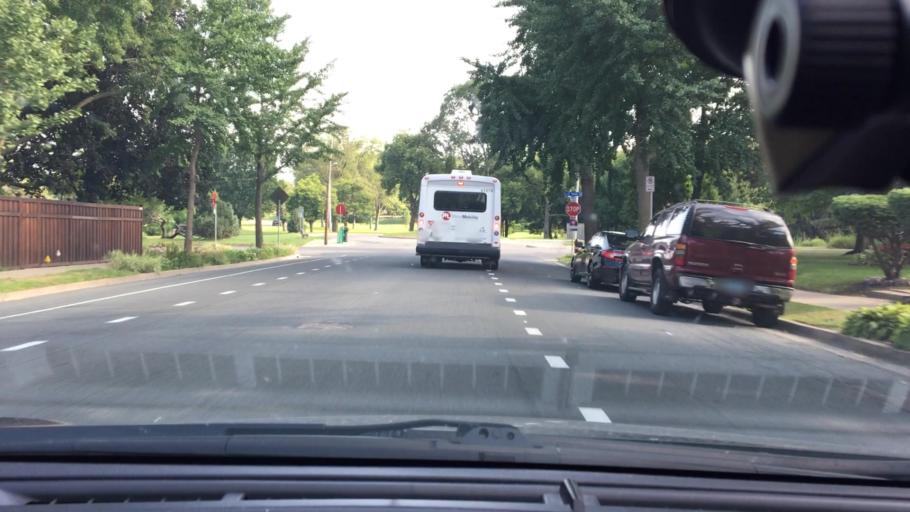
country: US
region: Minnesota
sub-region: Hennepin County
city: Richfield
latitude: 44.9058
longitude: -93.2526
